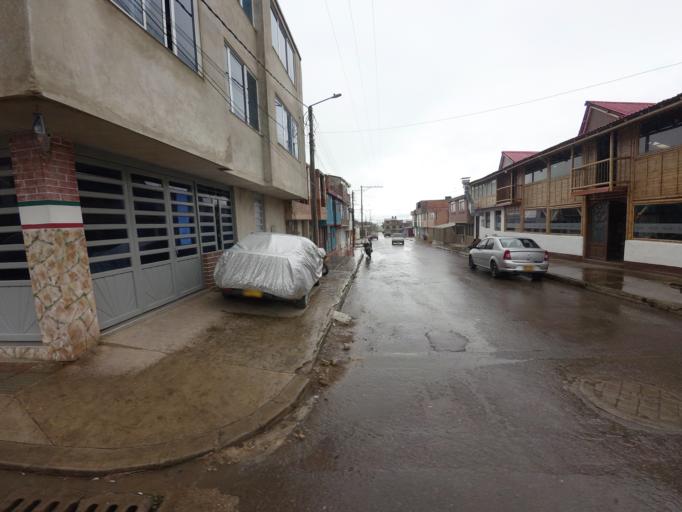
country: CO
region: Boyaca
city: Aquitania
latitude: 5.5206
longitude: -72.8840
